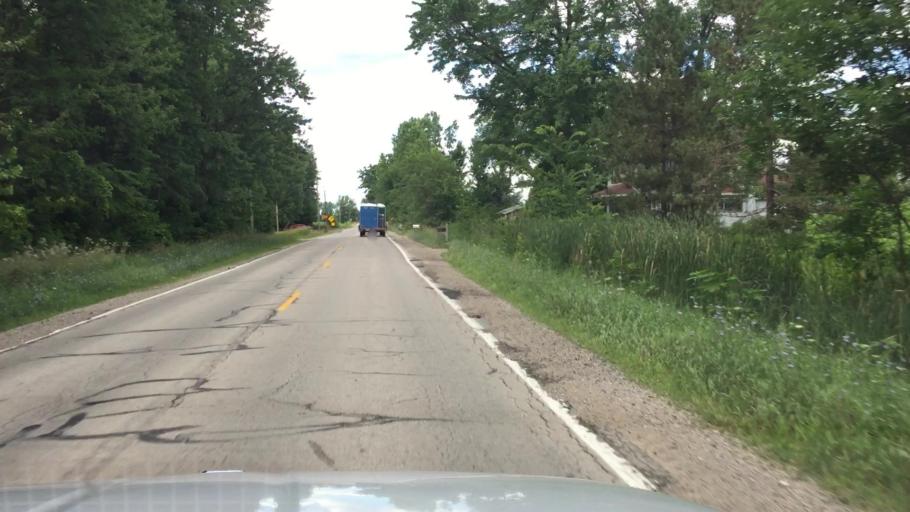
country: US
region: Michigan
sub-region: Saint Clair County
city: Capac
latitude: 42.9393
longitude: -82.9459
